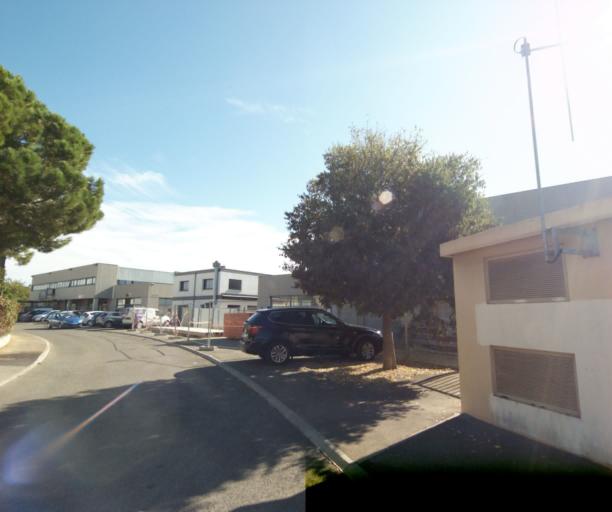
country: FR
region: Provence-Alpes-Cote d'Azur
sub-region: Departement des Bouches-du-Rhone
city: Saint-Victoret
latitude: 43.4180
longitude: 5.2413
